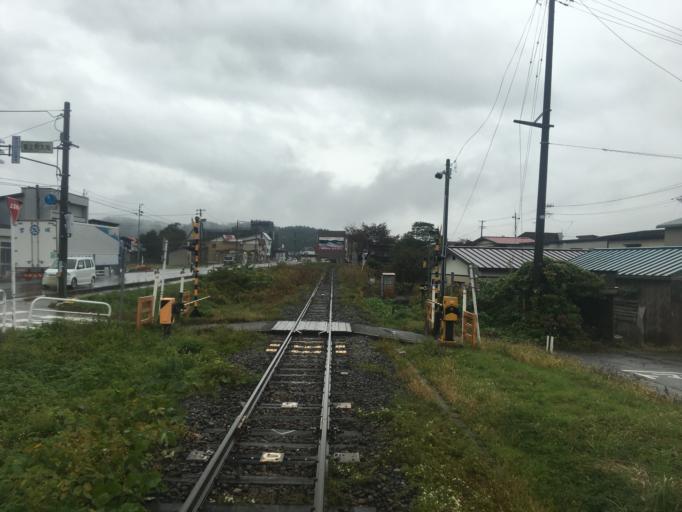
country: JP
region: Yamagata
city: Shinjo
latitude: 38.7661
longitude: 140.4770
